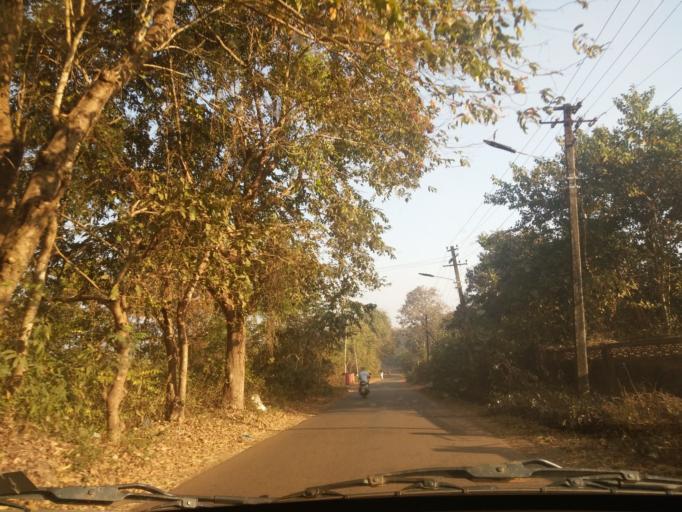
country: IN
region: Goa
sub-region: South Goa
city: Davorlim
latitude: 15.2816
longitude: 74.0065
